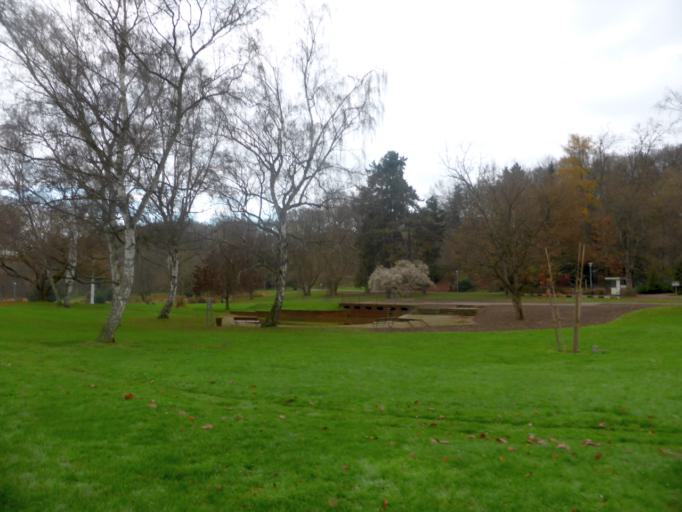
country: DE
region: Saarland
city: Saarbrucken
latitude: 49.2229
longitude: 6.9692
